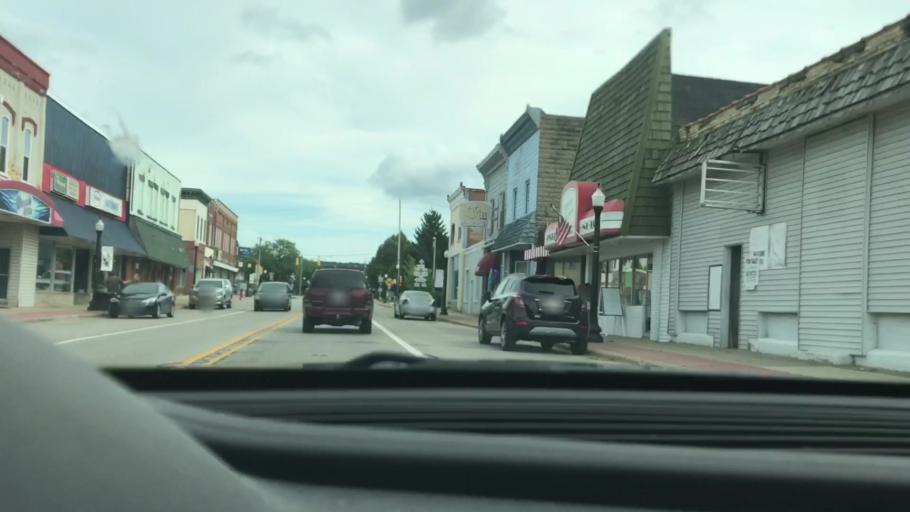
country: US
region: Michigan
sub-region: Antrim County
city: Mancelona
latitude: 44.9024
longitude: -85.0623
